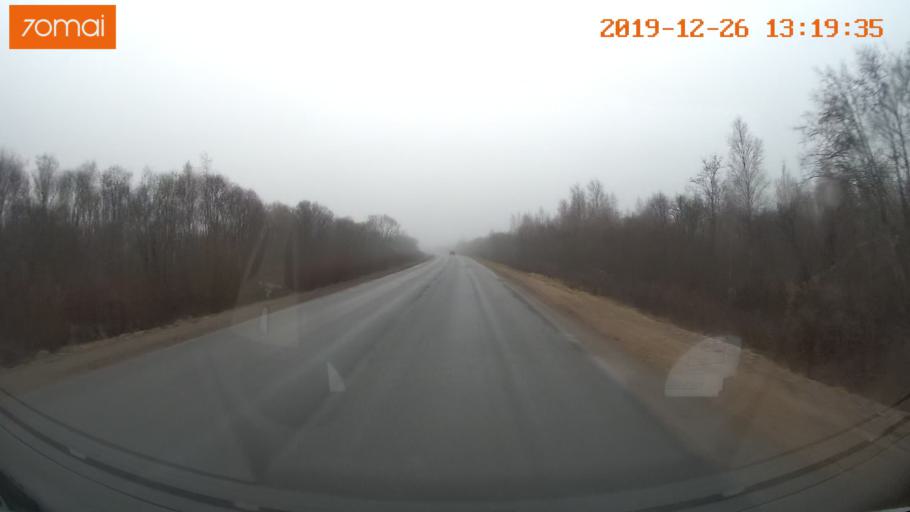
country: RU
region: Vologda
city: Cherepovets
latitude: 58.9389
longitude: 38.1322
